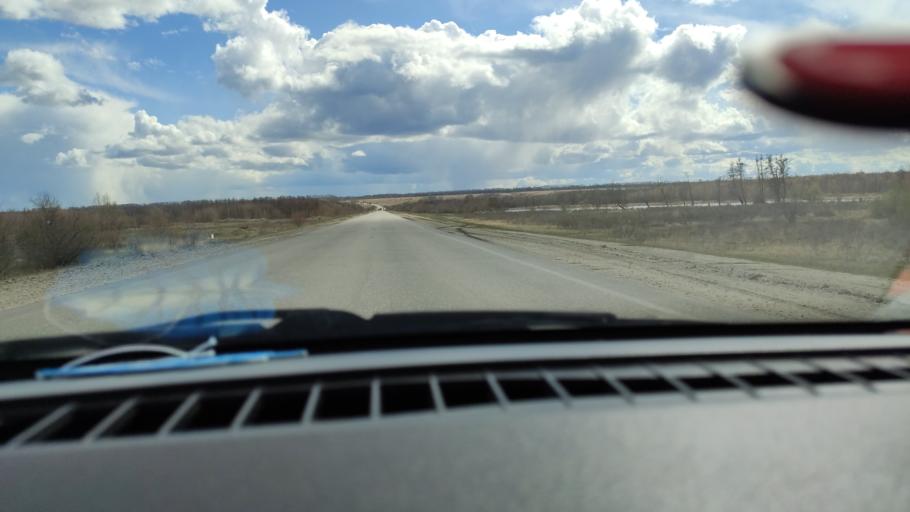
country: RU
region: Samara
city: Varlamovo
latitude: 53.1401
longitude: 48.2858
